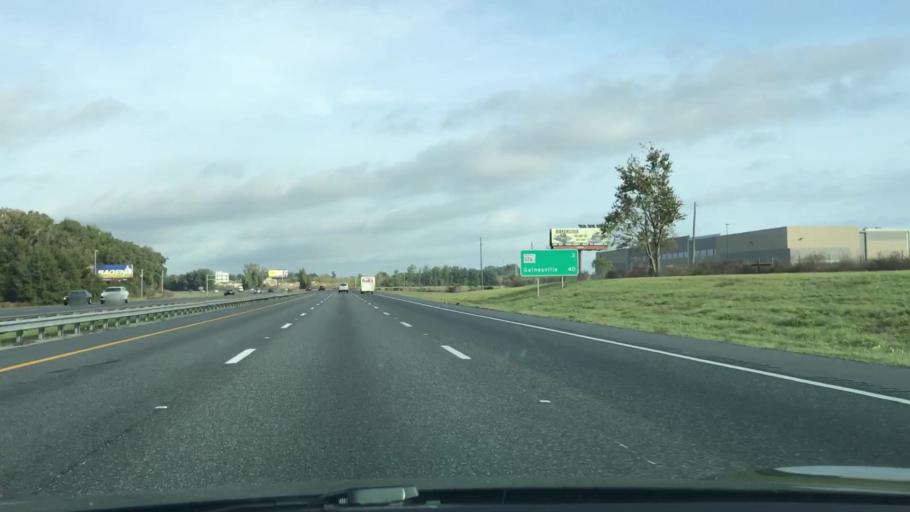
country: US
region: Florida
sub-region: Marion County
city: Ocala
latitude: 29.2213
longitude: -82.1873
